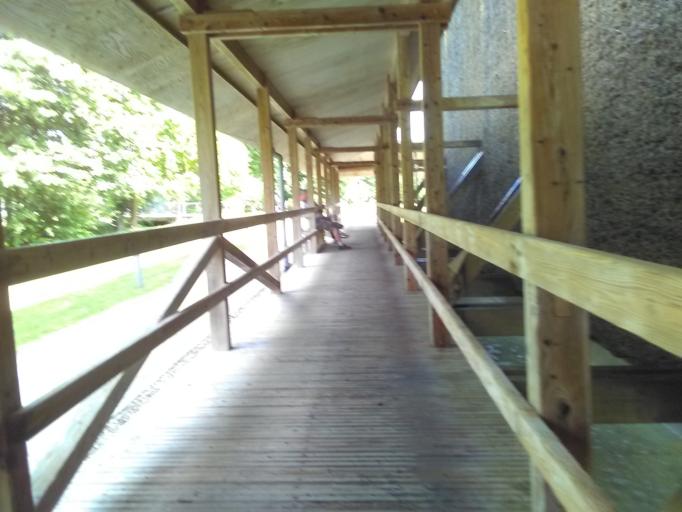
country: DE
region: Bavaria
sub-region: Upper Franconia
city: Bad Staffelstein
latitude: 50.1103
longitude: 10.9882
